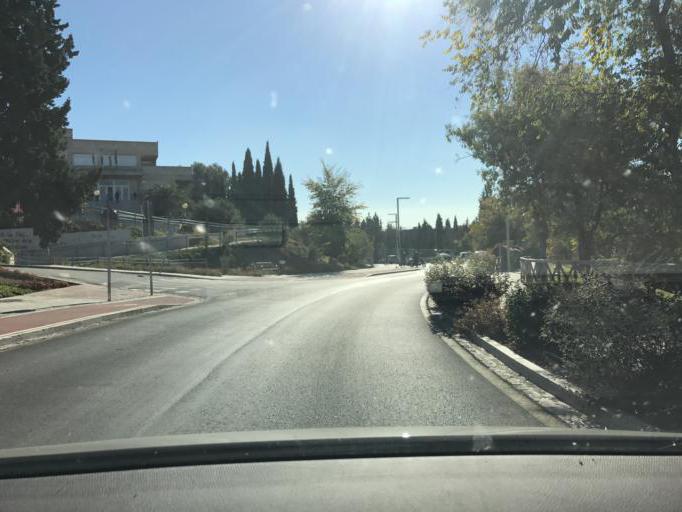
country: ES
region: Andalusia
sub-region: Provincia de Granada
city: Granada
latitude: 37.1930
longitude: -3.5949
